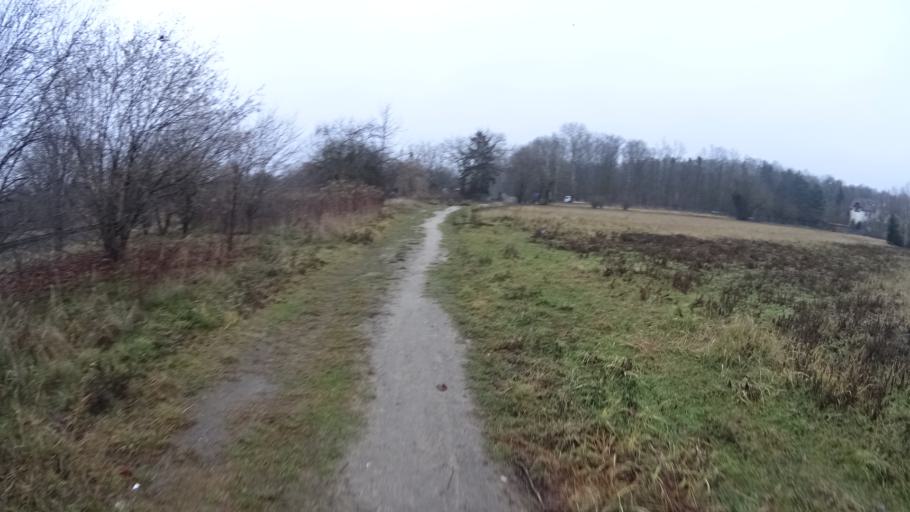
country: PL
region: Masovian Voivodeship
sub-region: Warszawa
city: Ursynow
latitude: 52.1394
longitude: 21.0305
